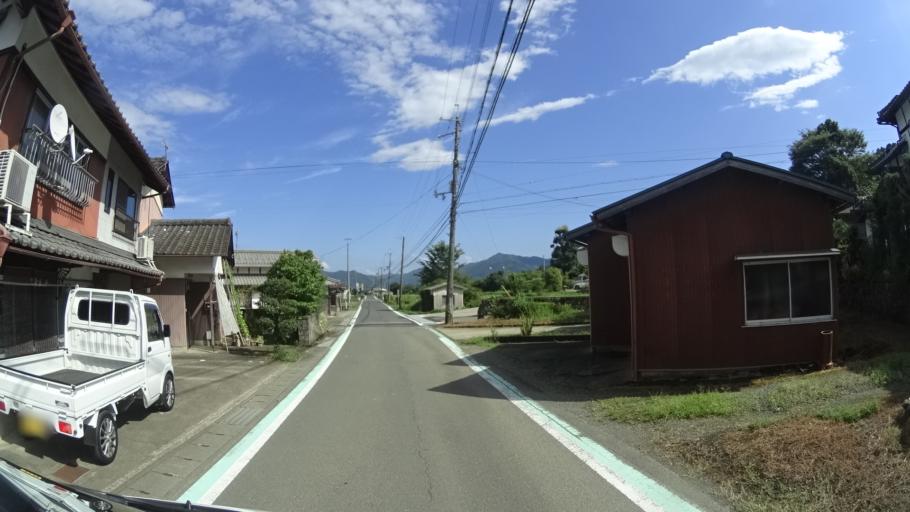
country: JP
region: Kyoto
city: Fukuchiyama
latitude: 35.3247
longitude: 135.1772
